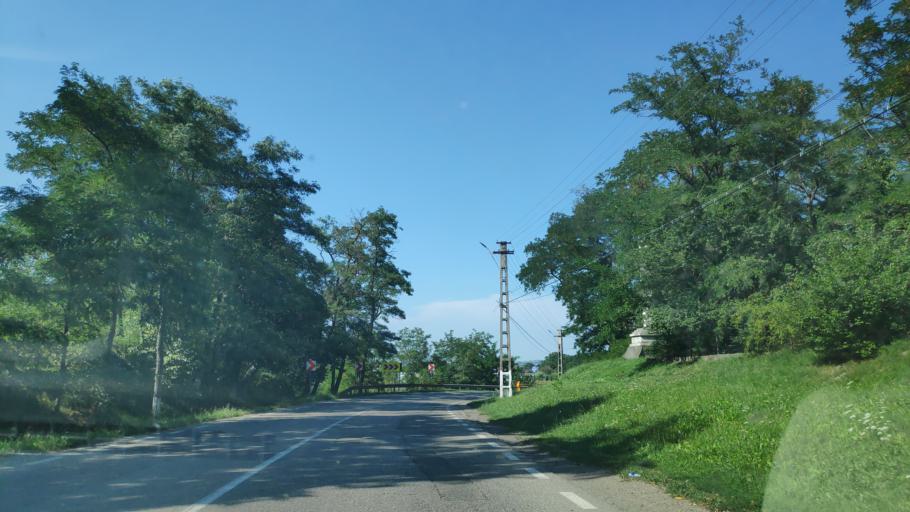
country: RO
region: Suceava
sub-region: Comuna Boroaia
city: Boroaia
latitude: 47.3506
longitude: 26.3353
